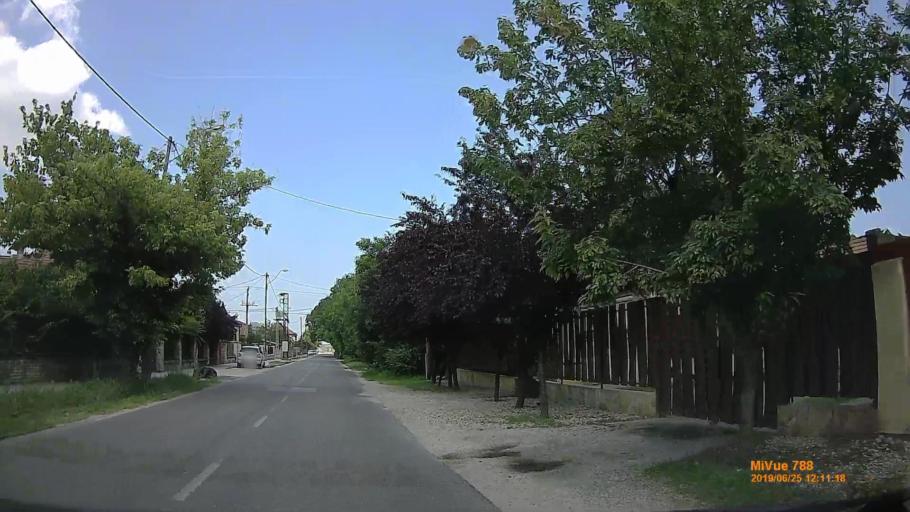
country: HU
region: Komarom-Esztergom
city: Dorog
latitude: 47.7397
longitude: 18.7225
